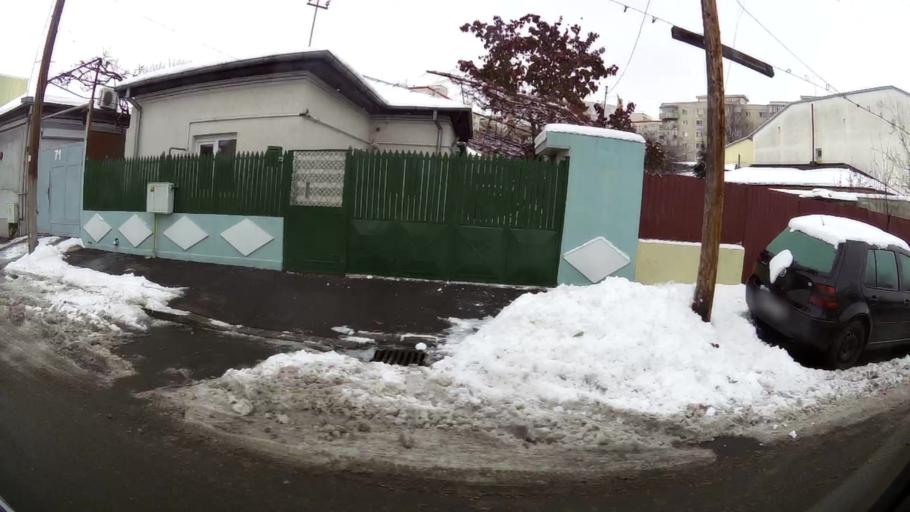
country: RO
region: Bucuresti
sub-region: Municipiul Bucuresti
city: Bucuresti
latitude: 44.3960
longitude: 26.1075
